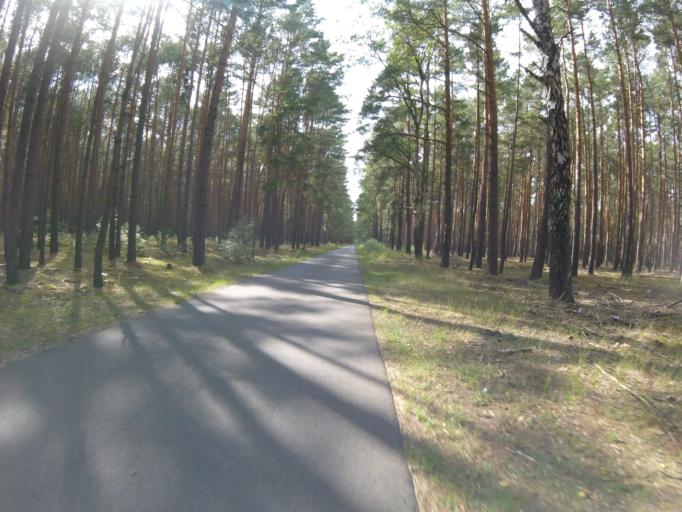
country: DE
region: Brandenburg
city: Halbe
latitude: 52.1694
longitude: 13.7592
